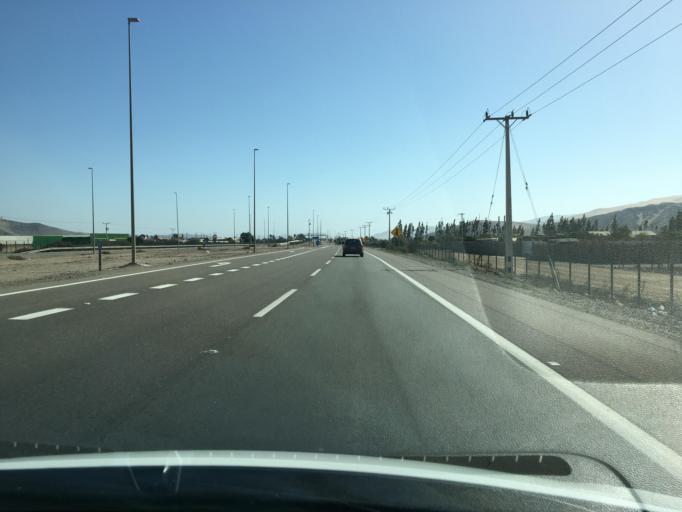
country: CL
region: Atacama
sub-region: Provincia de Copiapo
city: Copiapo
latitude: -27.3121
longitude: -70.5025
